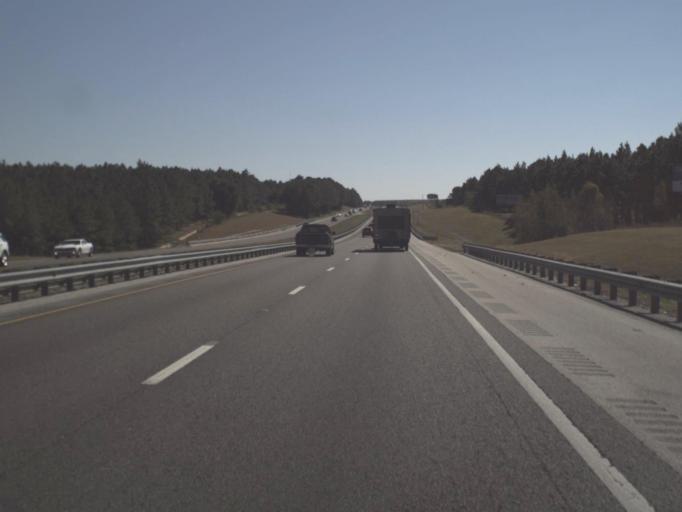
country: US
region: Florida
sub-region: Lake County
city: Minneola
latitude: 28.5908
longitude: -81.7124
